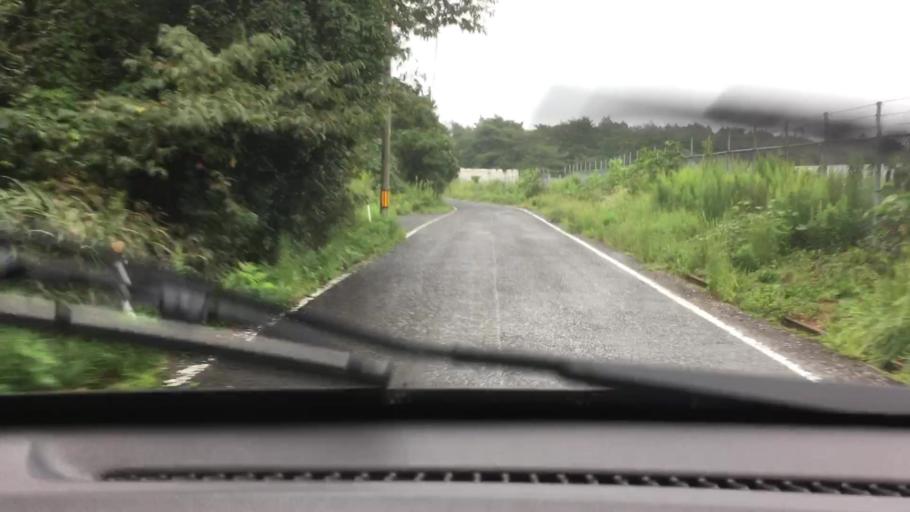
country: JP
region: Nagasaki
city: Togitsu
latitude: 32.9229
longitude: 129.7240
